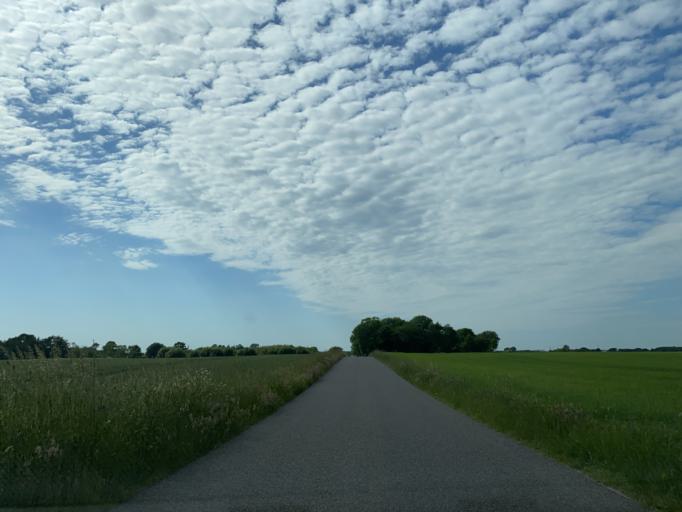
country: DK
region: Central Jutland
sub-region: Favrskov Kommune
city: Hammel
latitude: 56.2122
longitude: 9.8946
